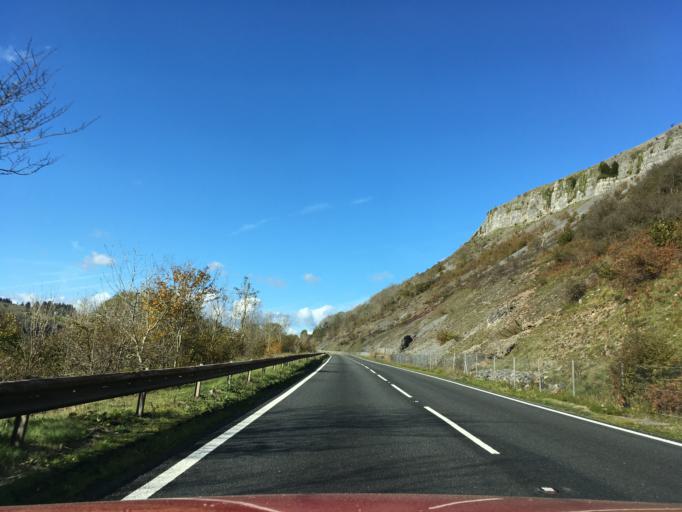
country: GB
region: Wales
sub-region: Merthyr Tydfil County Borough
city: Merthyr Tydfil
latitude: 51.7771
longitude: -3.4199
